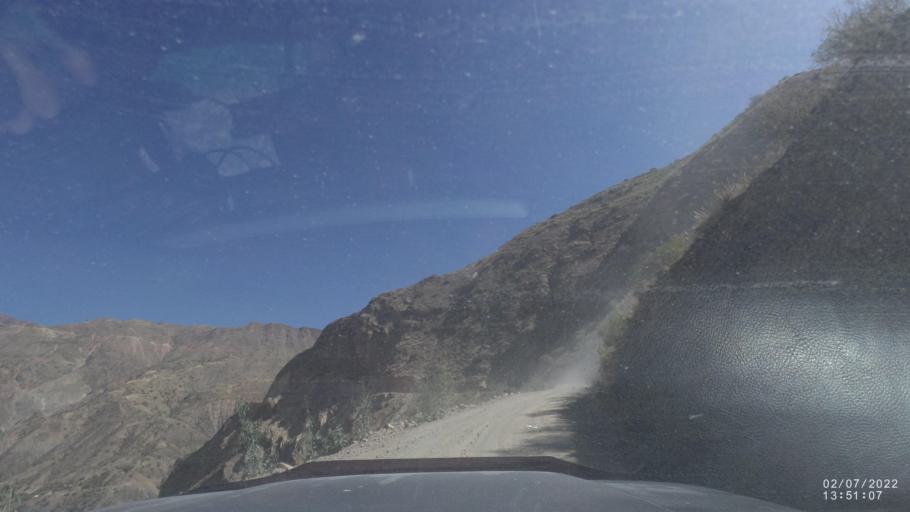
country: BO
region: Cochabamba
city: Irpa Irpa
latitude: -17.8221
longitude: -66.3807
